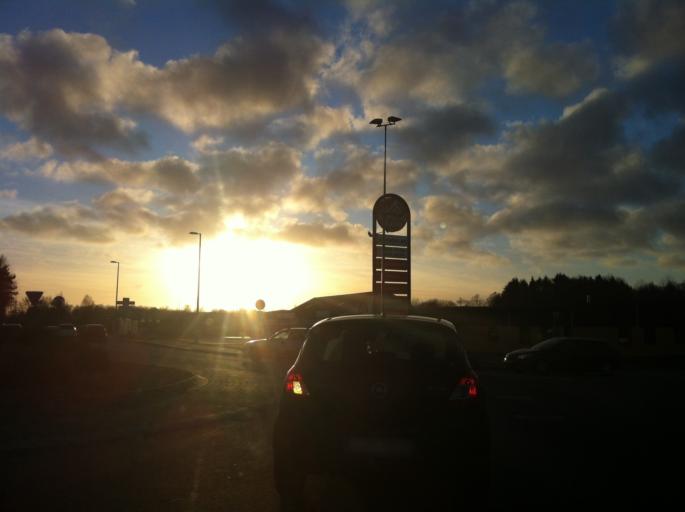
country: SE
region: Skane
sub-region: Hoors Kommun
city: Hoeoer
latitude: 55.9669
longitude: 13.5794
